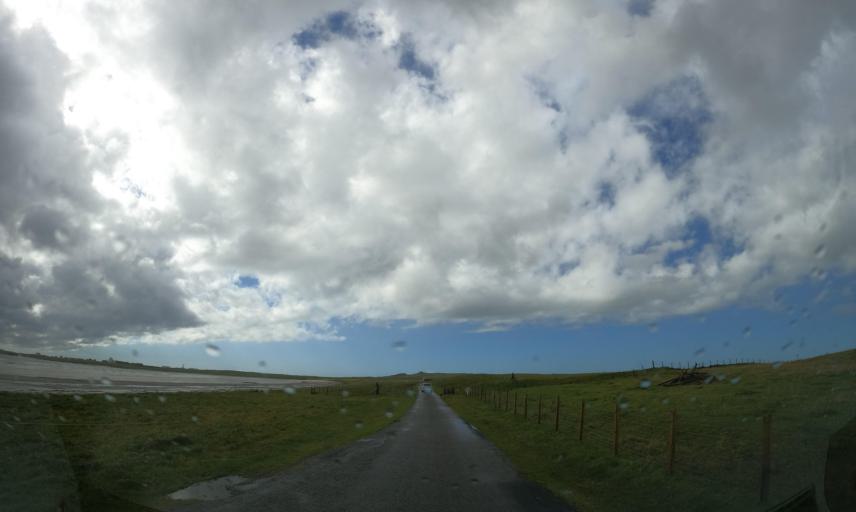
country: GB
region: Scotland
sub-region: Eilean Siar
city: Barra
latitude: 56.5181
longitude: -6.8128
